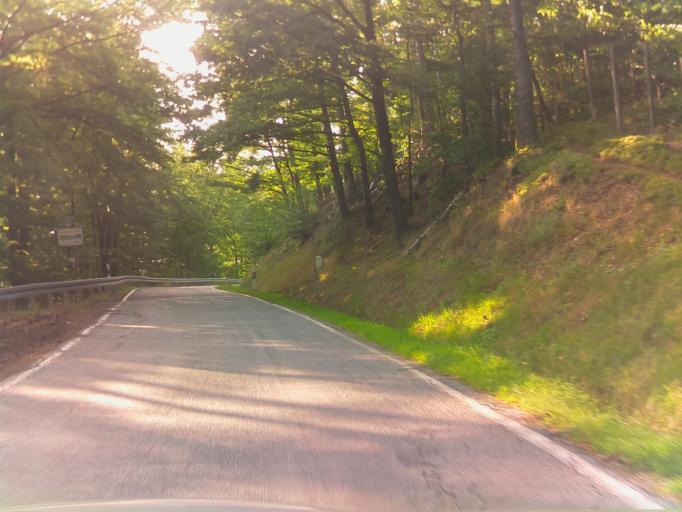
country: DE
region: Hesse
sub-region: Regierungsbezirk Darmstadt
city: Hesseneck
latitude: 49.5612
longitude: 9.1012
